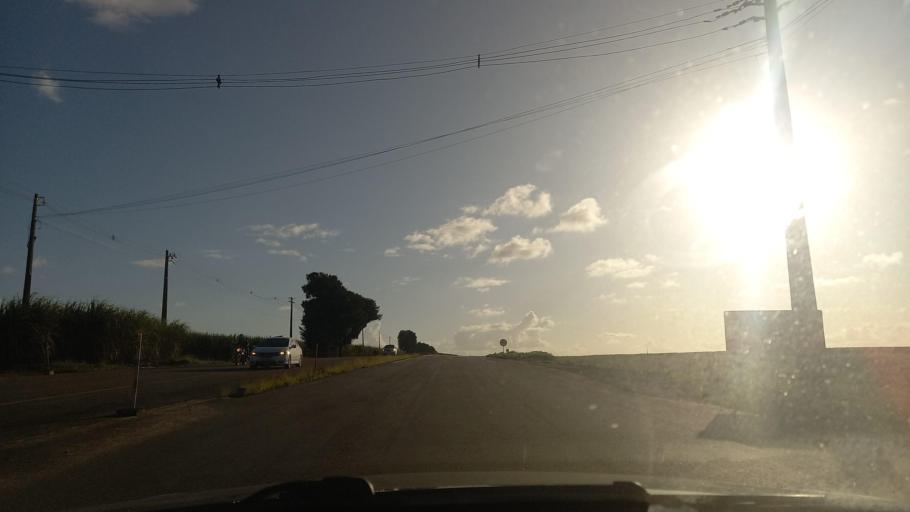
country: BR
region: Alagoas
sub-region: Campo Alegre
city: Campo Alegre
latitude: -9.8227
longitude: -36.2321
